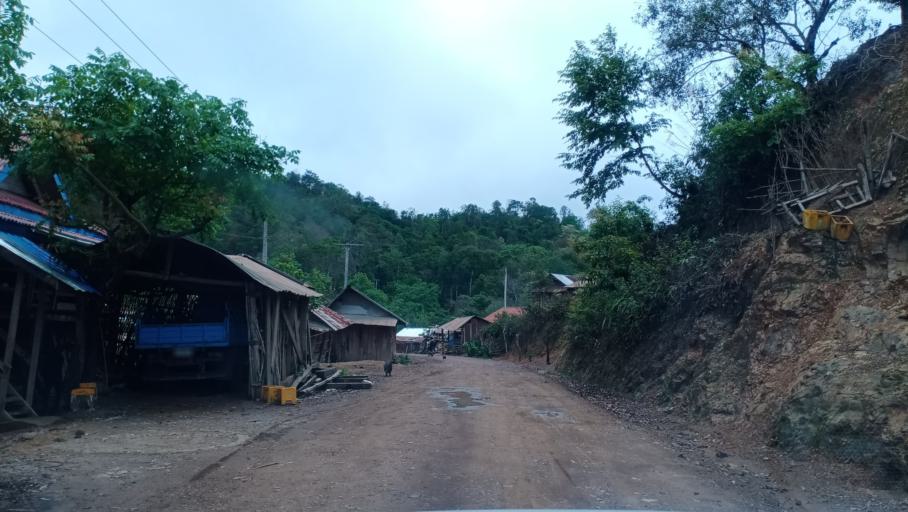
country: LA
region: Phongsali
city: Phongsali
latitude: 21.3460
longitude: 102.0930
